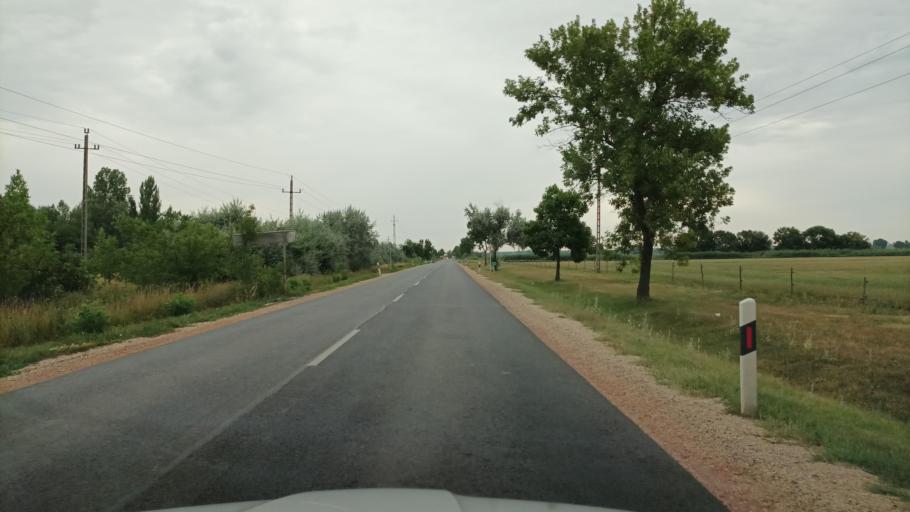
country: HU
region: Pest
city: Bugyi
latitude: 47.2364
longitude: 19.1870
